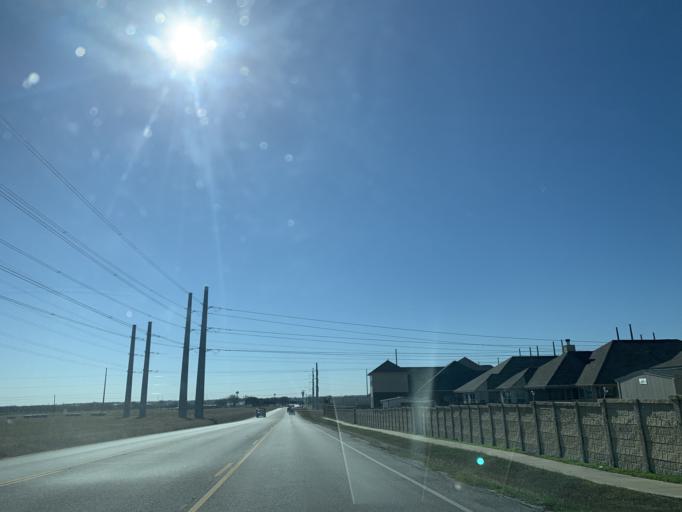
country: US
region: Texas
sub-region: Williamson County
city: Hutto
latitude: 30.5537
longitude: -97.5597
